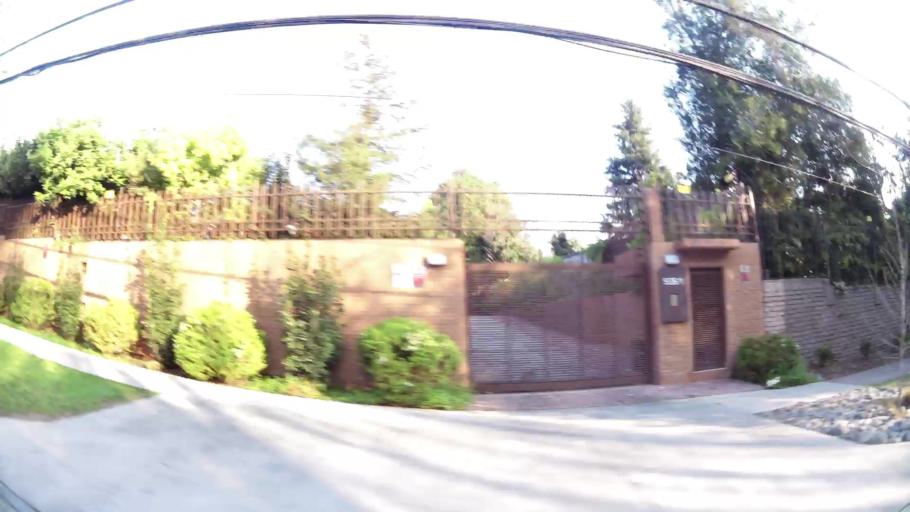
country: CL
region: Santiago Metropolitan
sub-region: Provincia de Santiago
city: Villa Presidente Frei, Nunoa, Santiago, Chile
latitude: -33.3918
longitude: -70.5317
